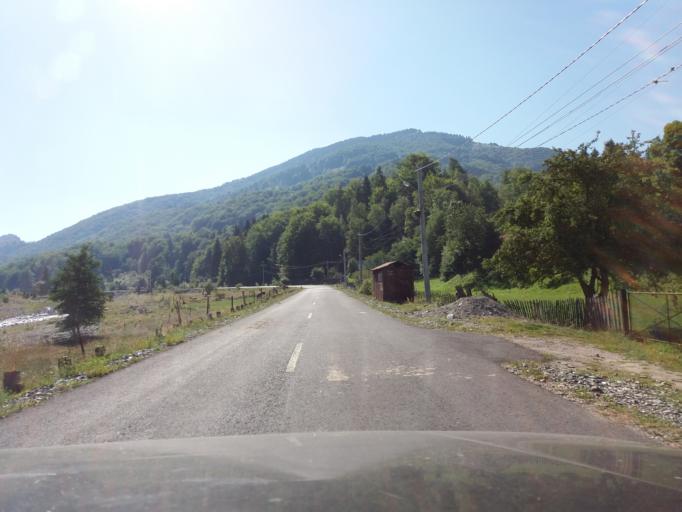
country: RO
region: Hunedoara
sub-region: Oras Petrila
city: Petrila
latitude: 45.4172
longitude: 23.4323
